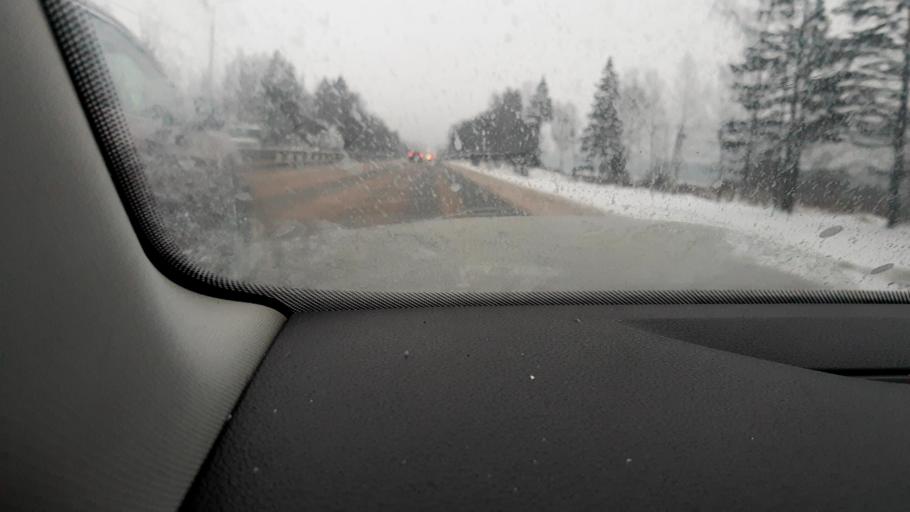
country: RU
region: Moskovskaya
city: Troitsk
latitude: 55.3309
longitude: 37.2836
